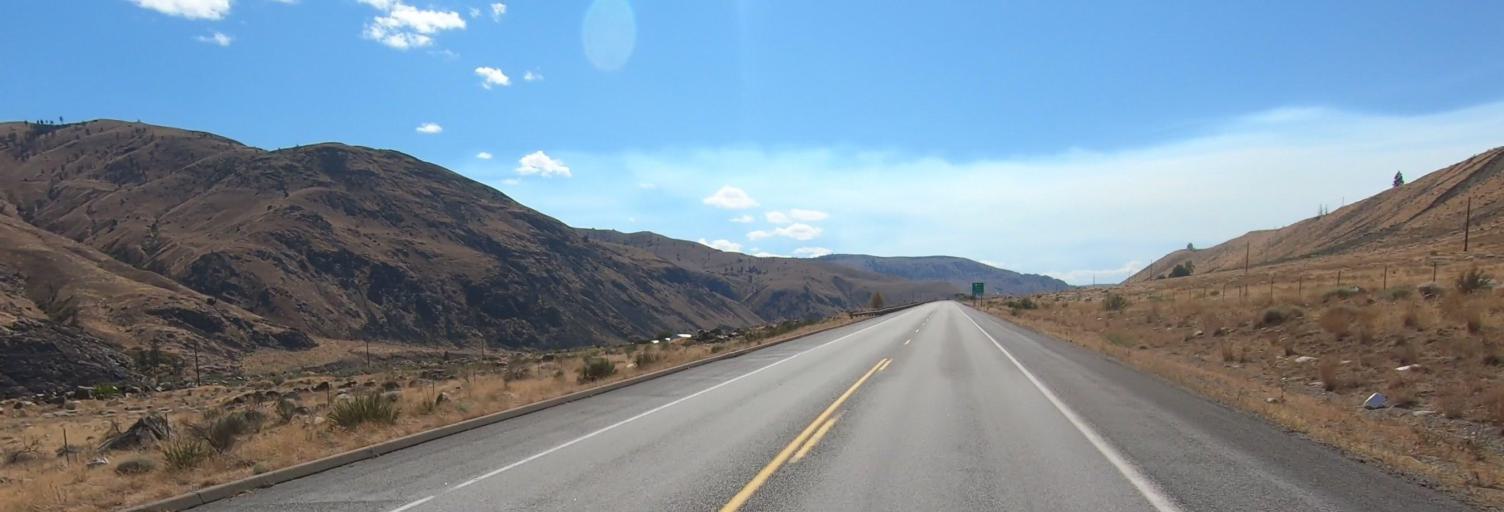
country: US
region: Washington
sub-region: Chelan County
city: Chelan
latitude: 47.8808
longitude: -119.9180
